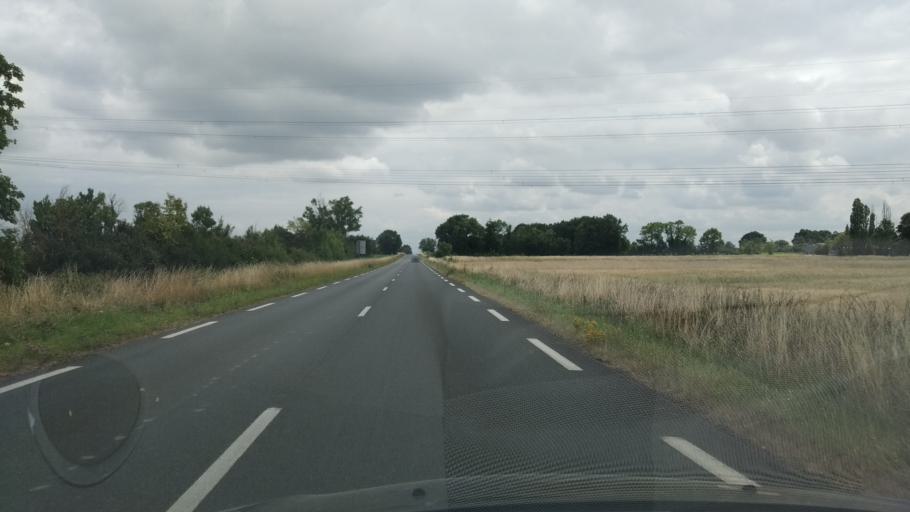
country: FR
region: Poitou-Charentes
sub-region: Departement de la Vienne
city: Saint-Maurice-la-Clouere
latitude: 46.3973
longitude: 0.3965
